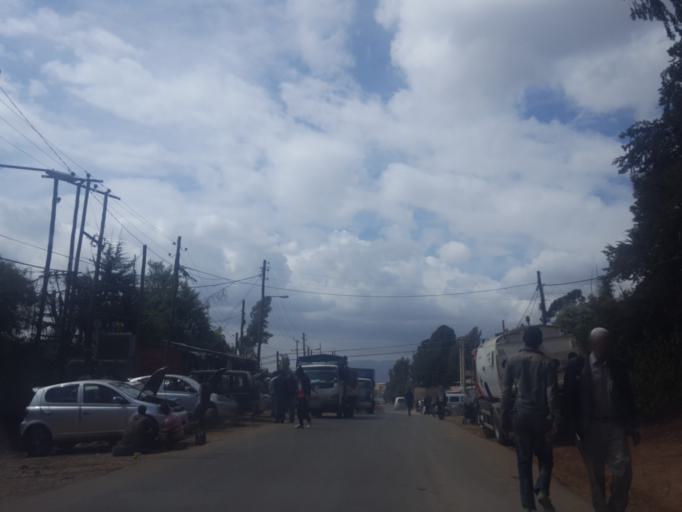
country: ET
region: Adis Abeba
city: Addis Ababa
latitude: 9.0638
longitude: 38.7446
